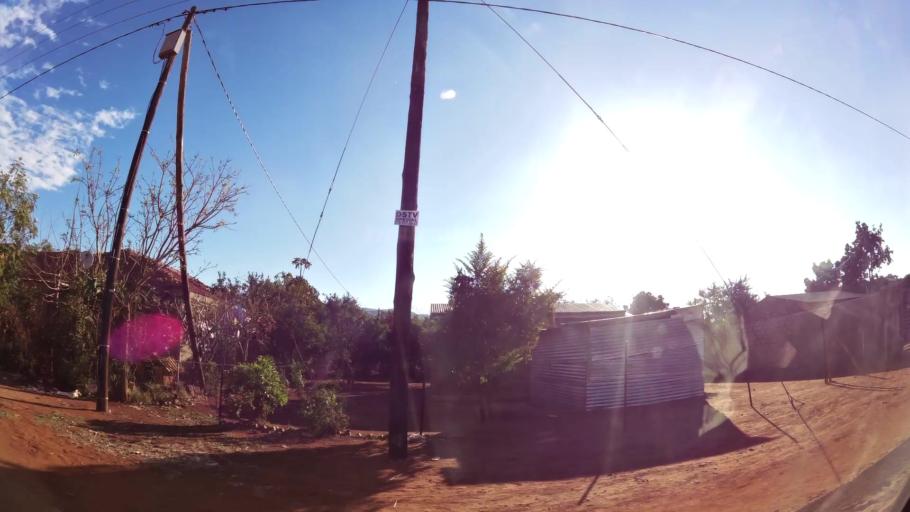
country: ZA
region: Limpopo
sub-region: Waterberg District Municipality
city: Mokopane
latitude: -24.1808
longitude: 28.9775
